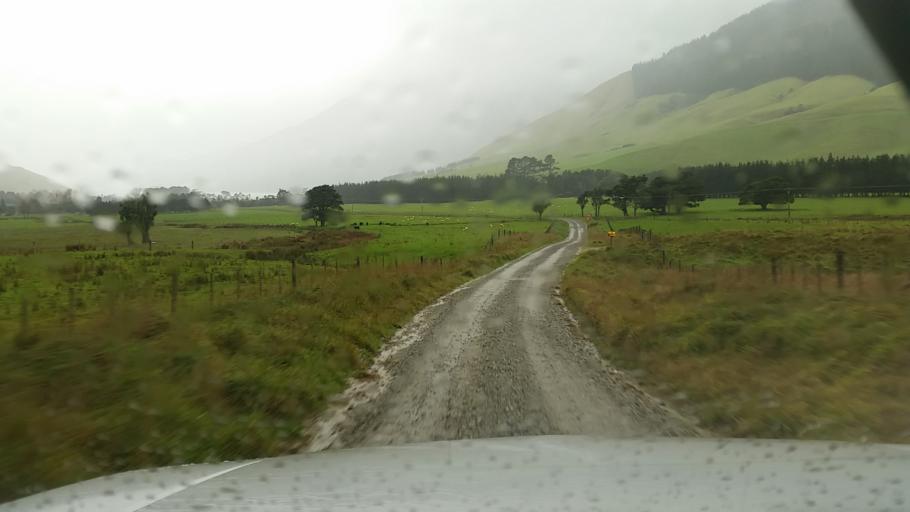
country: NZ
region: Marlborough
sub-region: Marlborough District
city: Picton
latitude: -41.1296
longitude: 174.0394
